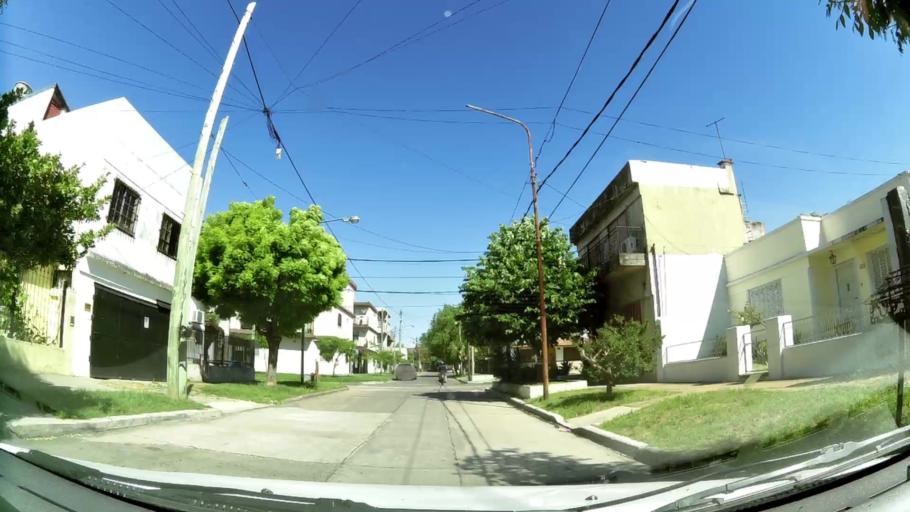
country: AR
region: Buenos Aires
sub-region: Partido de General San Martin
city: General San Martin
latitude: -34.5387
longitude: -58.5728
